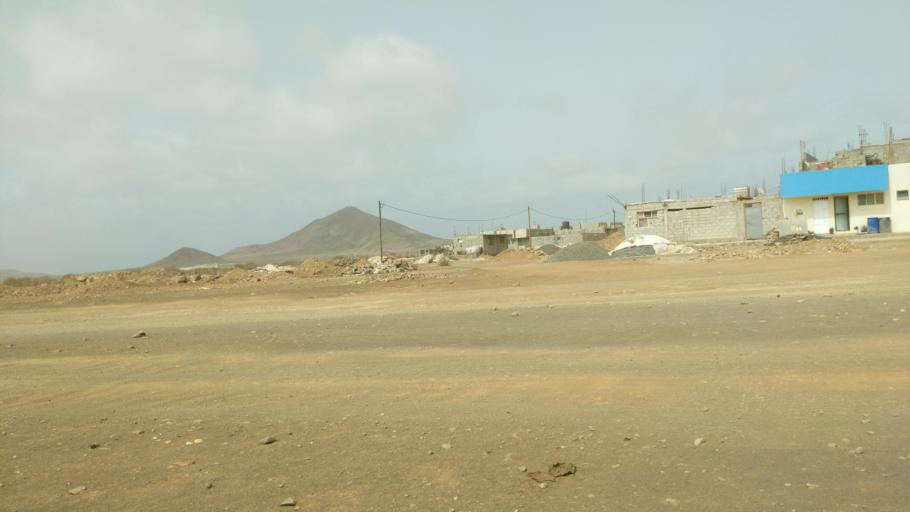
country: CV
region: Sal
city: Espargos
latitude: 16.7678
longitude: -22.9451
